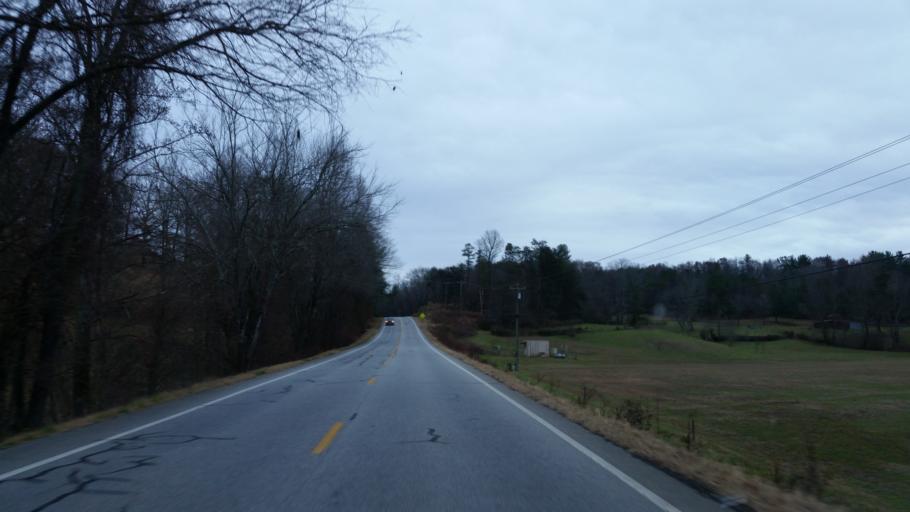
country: US
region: Georgia
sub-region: Dawson County
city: Dawsonville
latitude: 34.5230
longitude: -84.2497
